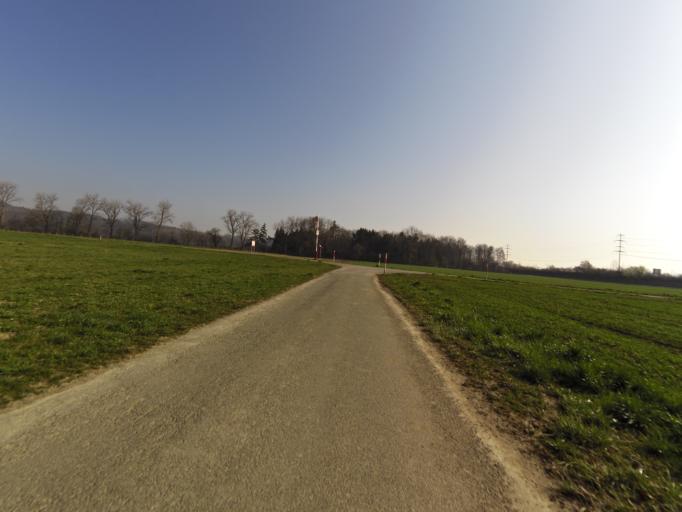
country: CH
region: Thurgau
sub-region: Frauenfeld District
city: Frauenfeld
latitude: 47.5775
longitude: 8.9188
